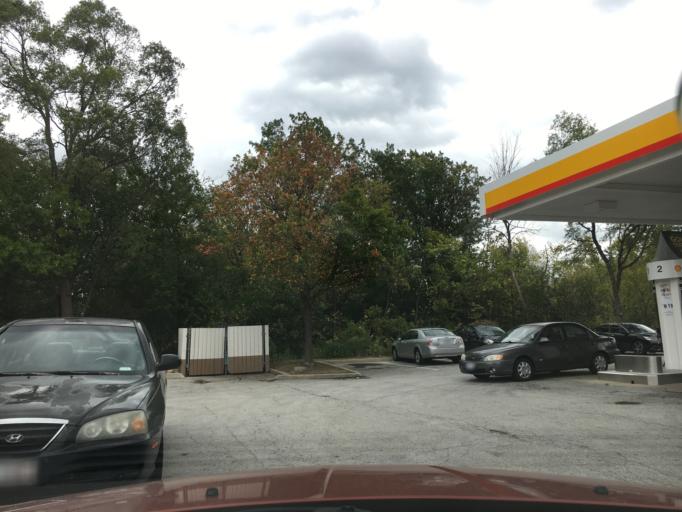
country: US
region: Illinois
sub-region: Cook County
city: Tinley Park
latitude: 41.6029
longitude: -87.7848
